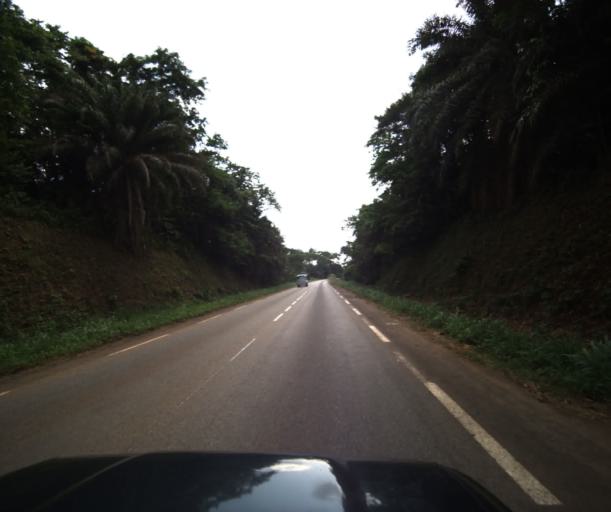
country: CM
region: Centre
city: Eseka
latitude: 3.8712
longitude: 10.6395
